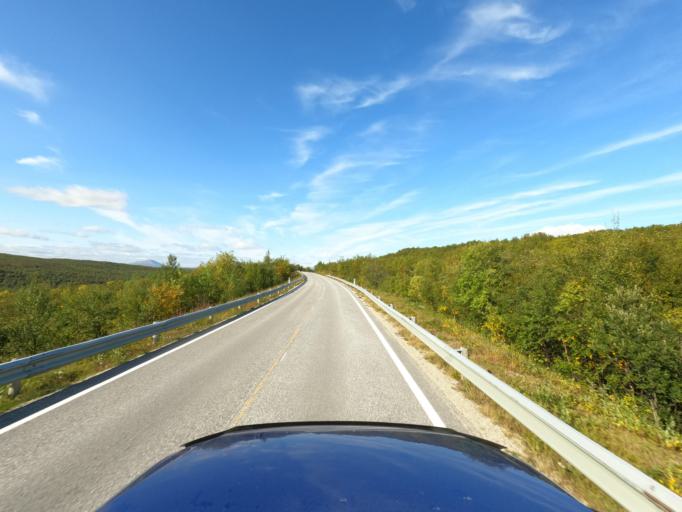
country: NO
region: Finnmark Fylke
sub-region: Porsanger
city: Lakselv
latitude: 69.7665
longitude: 25.1756
